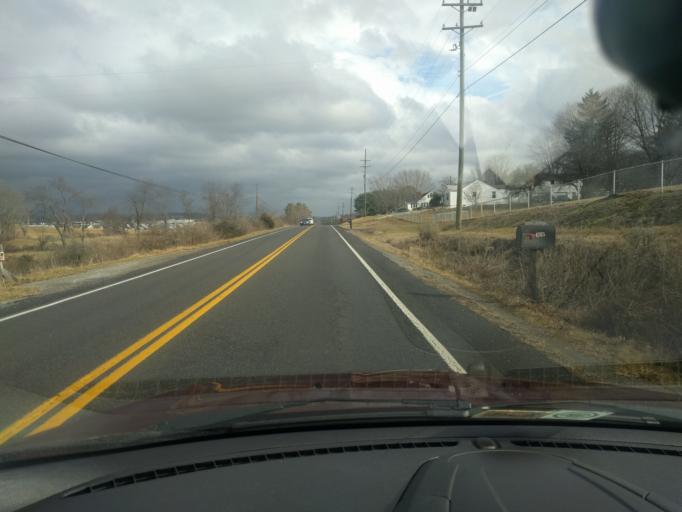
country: US
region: Virginia
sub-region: Pulaski County
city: Dublin
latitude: 37.0661
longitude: -80.7159
